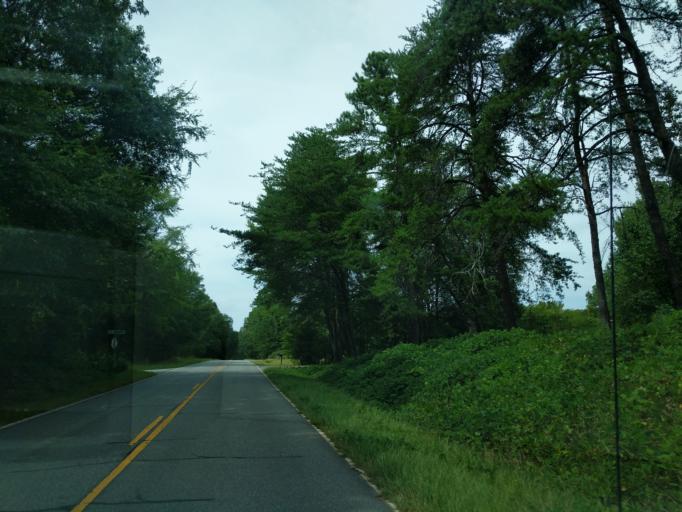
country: US
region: South Carolina
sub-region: Abbeville County
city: Calhoun Falls
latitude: 34.1356
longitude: -82.5940
